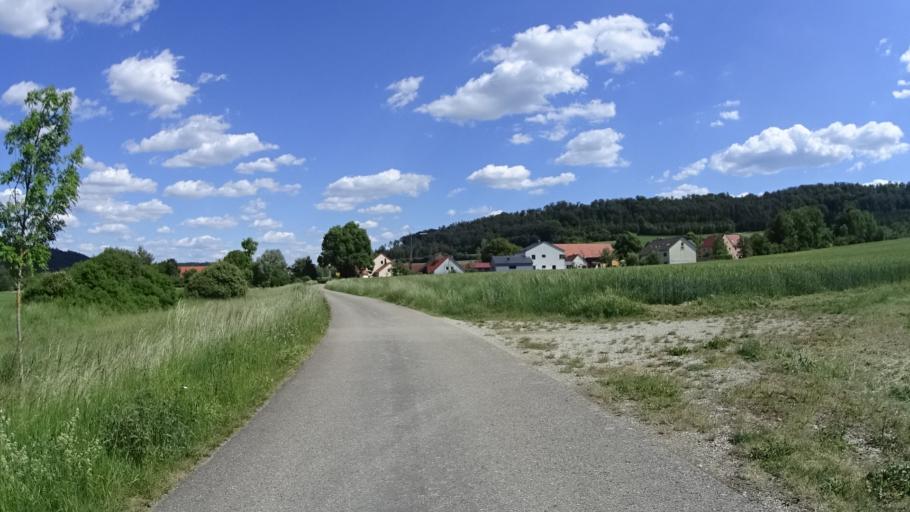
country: DE
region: Bavaria
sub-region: Regierungsbezirk Mittelfranken
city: Greding
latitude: 49.0655
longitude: 11.3060
